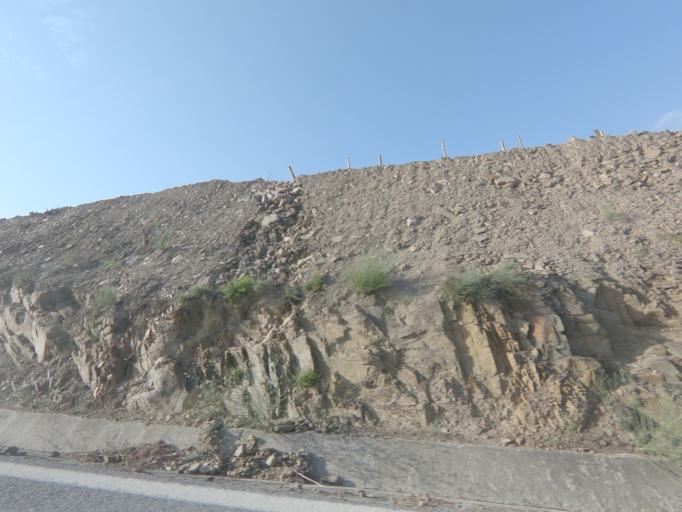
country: PT
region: Viseu
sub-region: Tabuaco
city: Tabuaco
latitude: 41.1400
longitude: -7.5450
